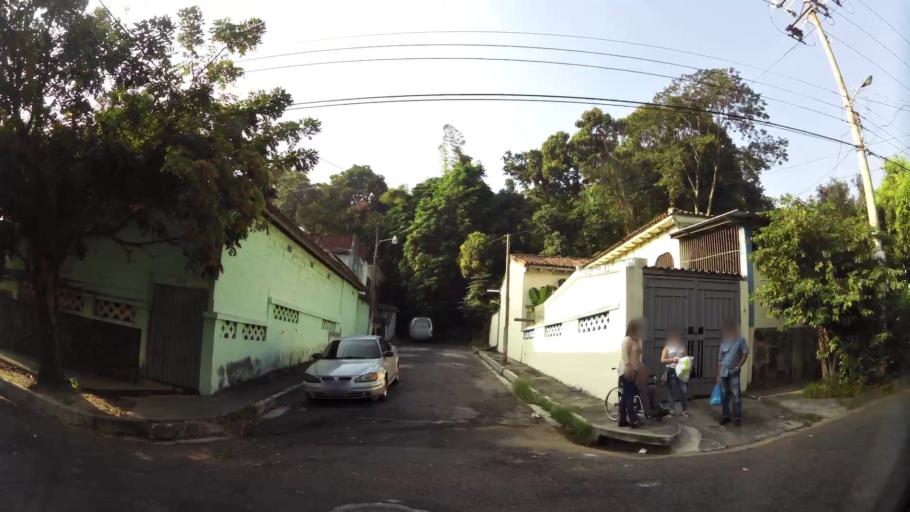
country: SV
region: San Salvador
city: San Salvador
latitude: 13.6809
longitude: -89.2021
